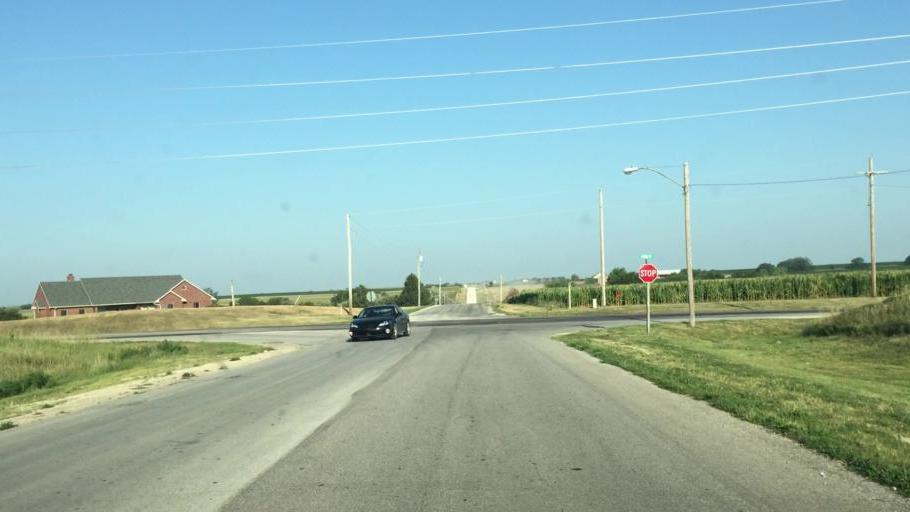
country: US
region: Kansas
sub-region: Nemaha County
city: Sabetha
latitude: 39.8856
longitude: -95.7877
